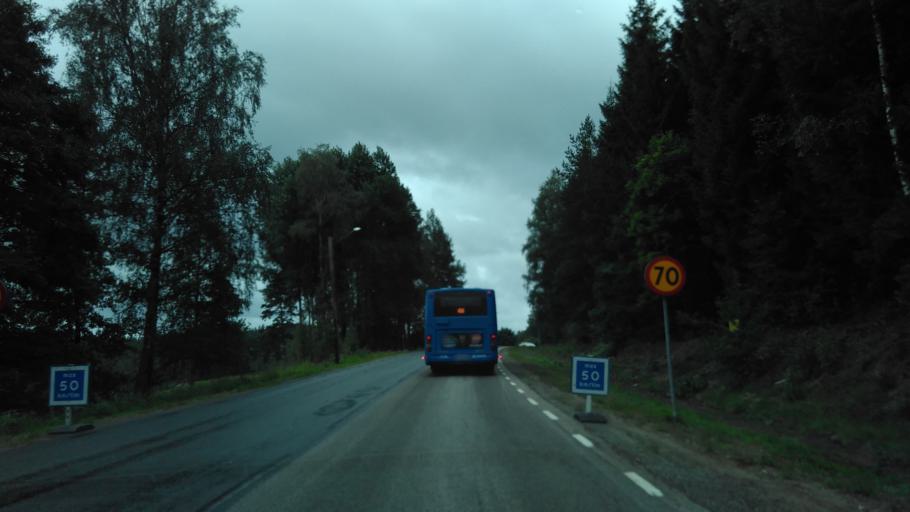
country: SE
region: Vaestra Goetaland
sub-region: Marks Kommun
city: Fritsla
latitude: 57.5638
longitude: 12.8111
